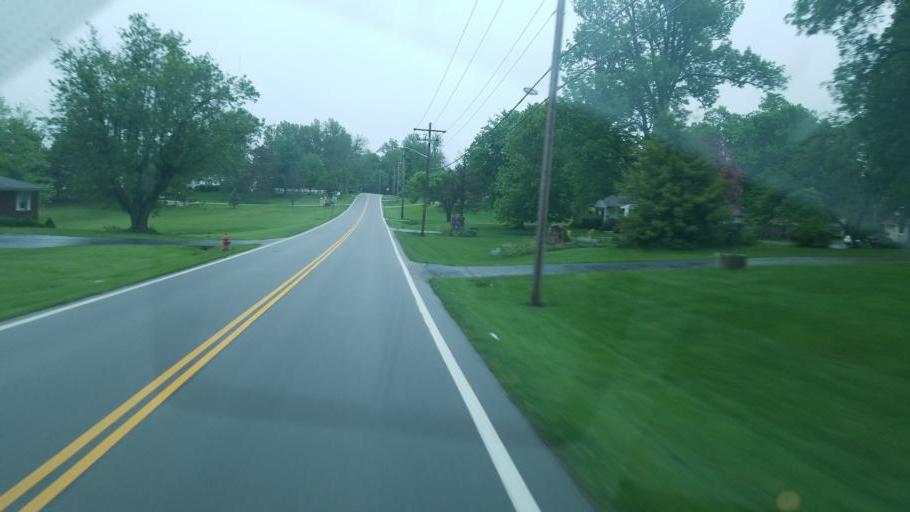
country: US
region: Ohio
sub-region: Highland County
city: Hillsboro
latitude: 39.1997
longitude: -83.6248
